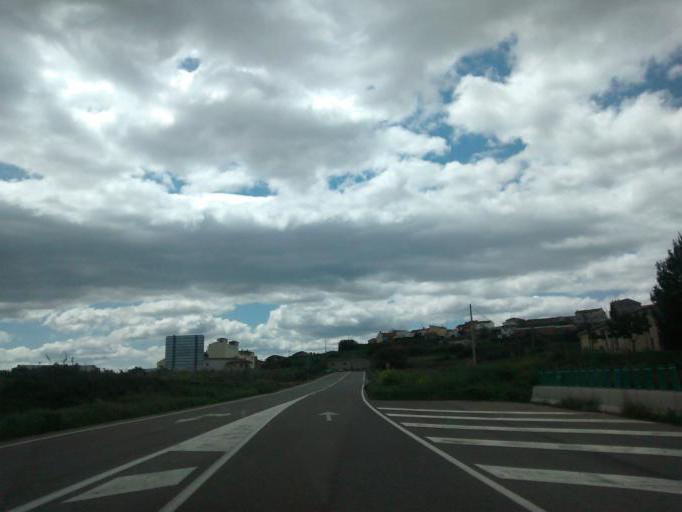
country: ES
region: La Rioja
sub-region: Provincia de La Rioja
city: Pradejon
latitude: 42.3242
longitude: -2.0916
